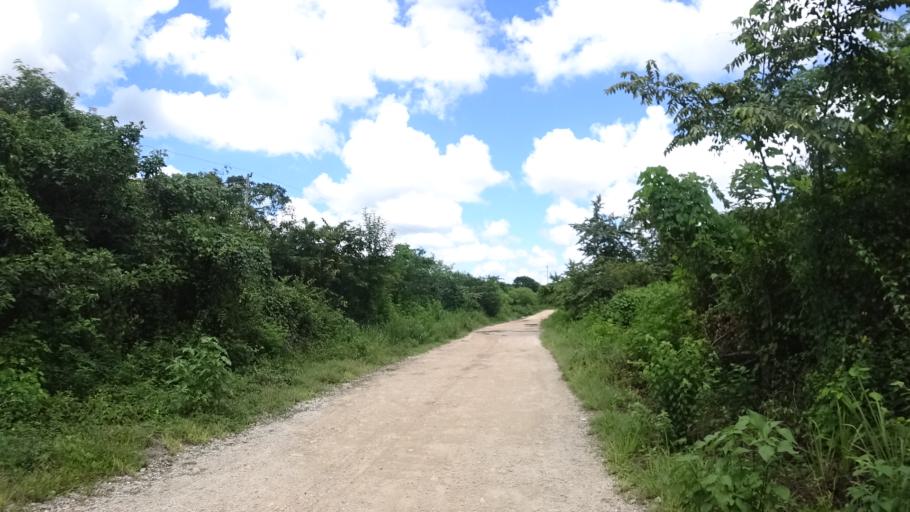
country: MX
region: Yucatan
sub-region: Valladolid
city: Dzitnup
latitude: 20.6697
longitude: -88.2289
